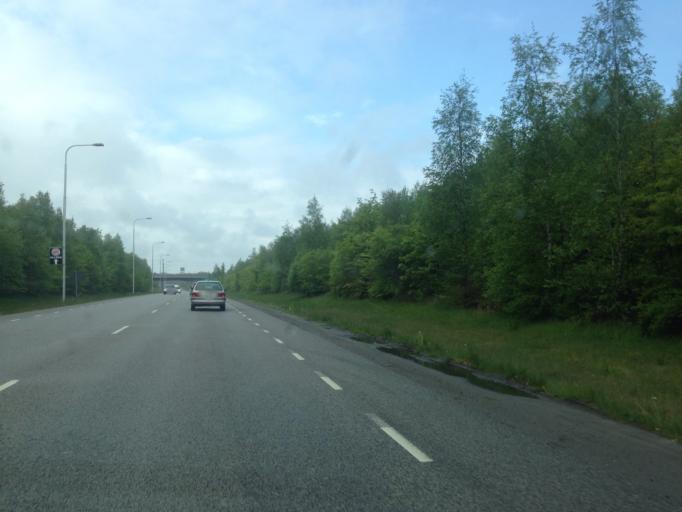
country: SE
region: Skane
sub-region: Malmo
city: Bunkeflostrand
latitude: 55.5613
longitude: 12.9620
